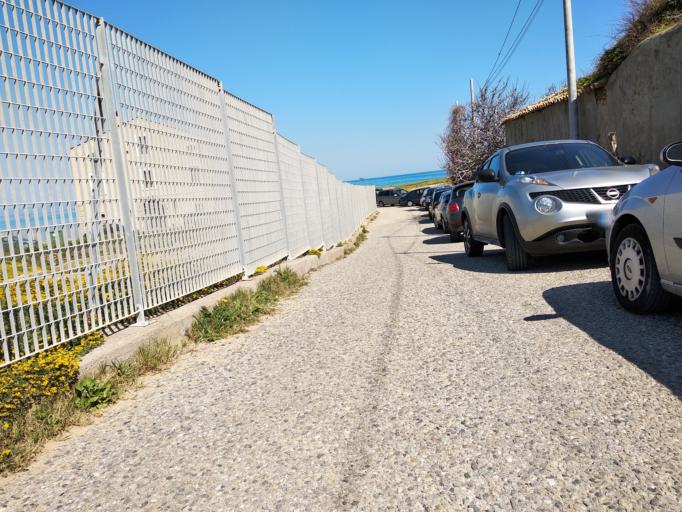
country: IT
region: Calabria
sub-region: Provincia di Crotone
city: Crotone
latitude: 39.0281
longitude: 17.2049
